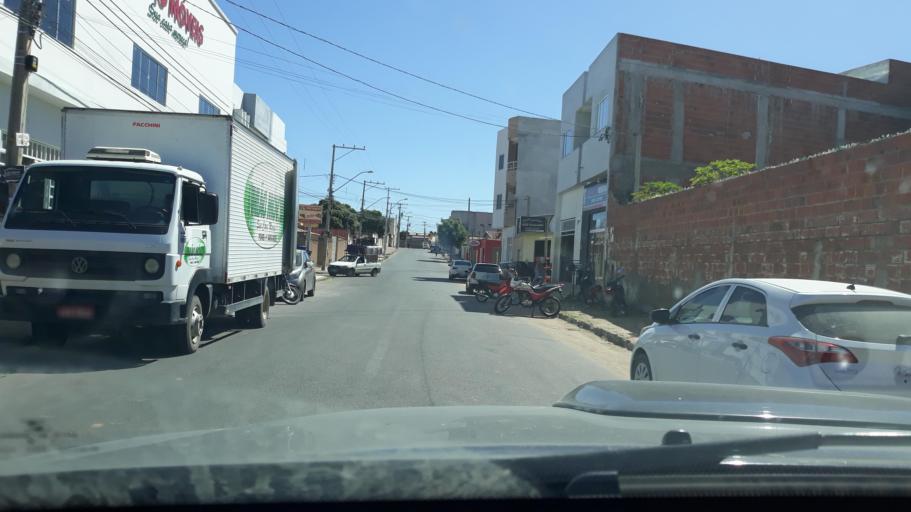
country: BR
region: Bahia
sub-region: Guanambi
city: Guanambi
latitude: -14.2201
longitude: -42.7943
